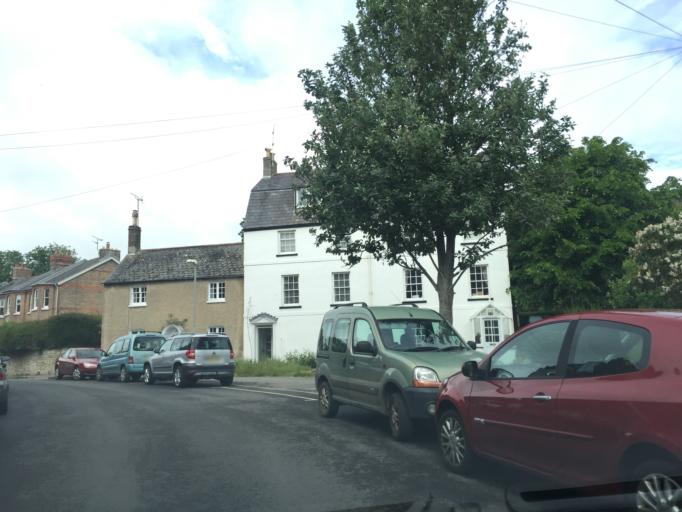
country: GB
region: England
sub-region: Dorset
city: Dorchester
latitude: 50.7134
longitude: -2.4295
